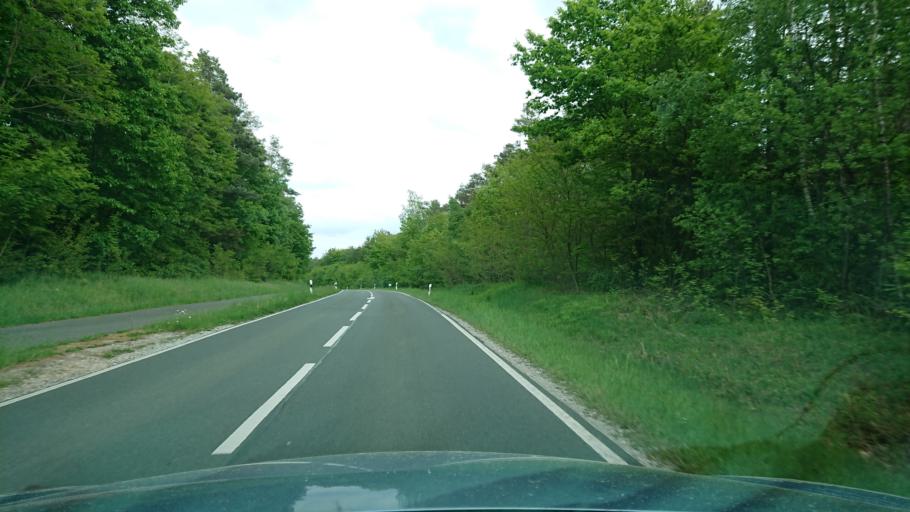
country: DE
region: Bavaria
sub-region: Regierungsbezirk Mittelfranken
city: Rottenbach
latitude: 49.6683
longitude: 10.9383
